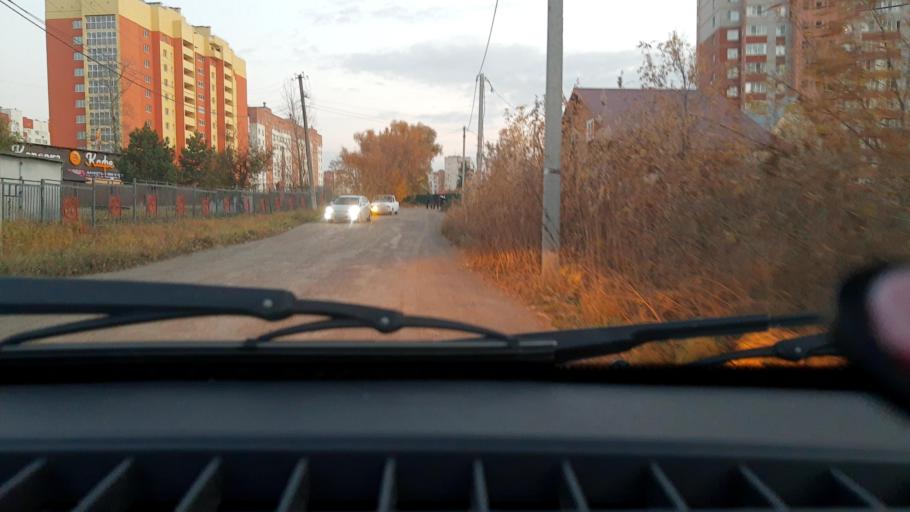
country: RU
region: Bashkortostan
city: Mikhaylovka
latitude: 54.7146
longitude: 55.8295
